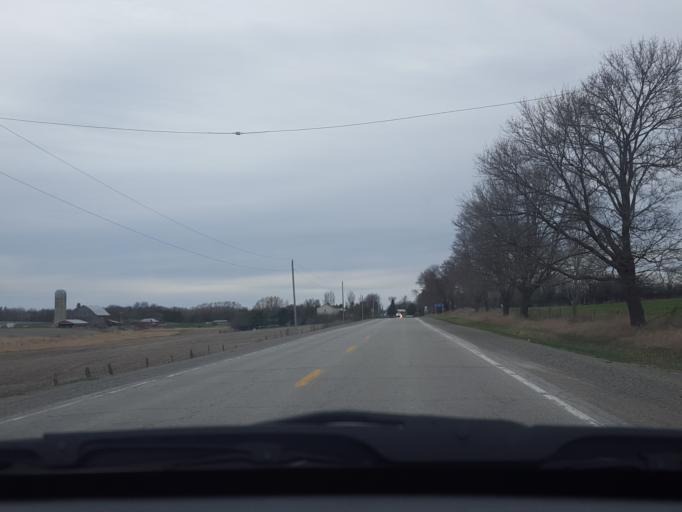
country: CA
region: Ontario
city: Uxbridge
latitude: 44.2559
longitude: -79.1333
